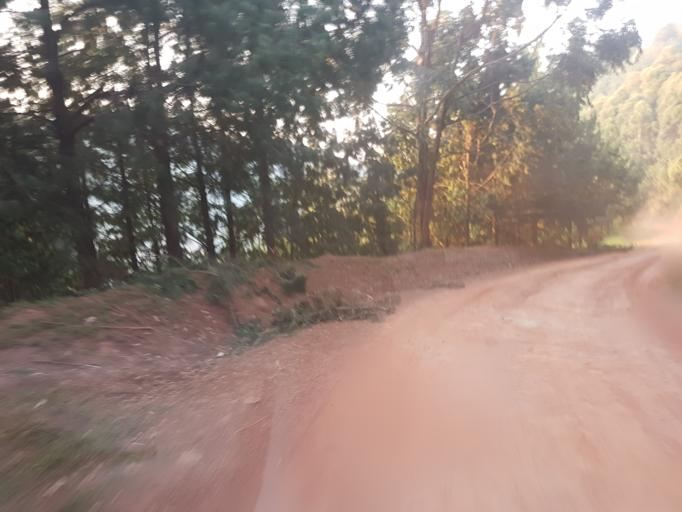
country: UG
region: Western Region
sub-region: Kanungu District
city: Kanungu
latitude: -1.0066
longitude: 29.8449
